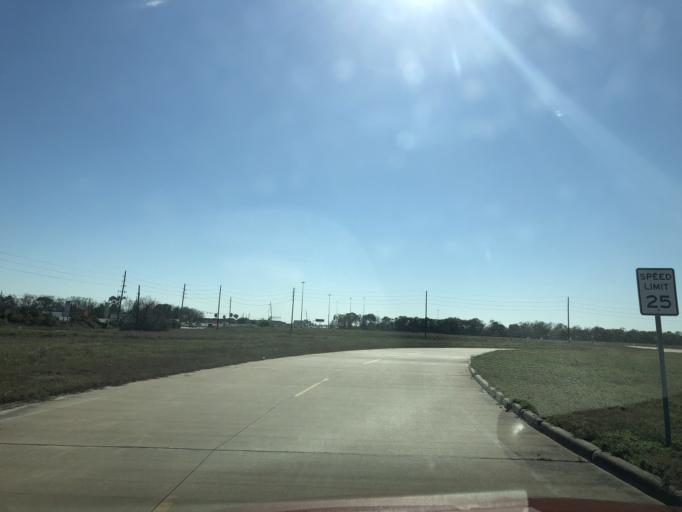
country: US
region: Texas
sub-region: Brazoria County
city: Brookside Village
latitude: 29.5904
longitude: -95.3878
